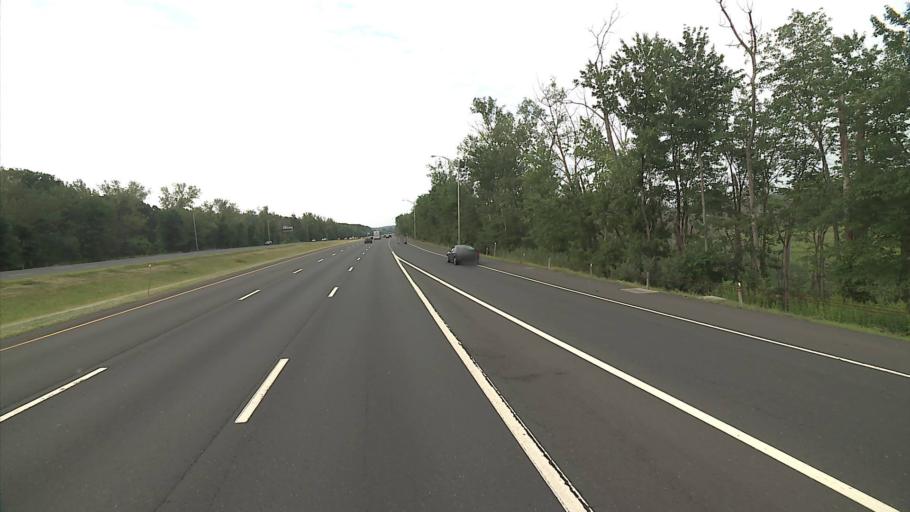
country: US
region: Connecticut
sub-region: Hartford County
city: Farmington
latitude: 41.7026
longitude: -72.8049
